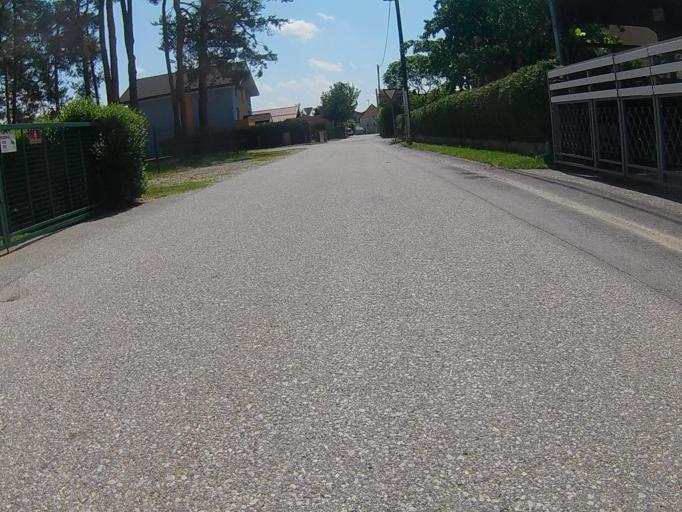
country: SI
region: Miklavz na Dravskem Polju
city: Miklavz na Dravskem Polju
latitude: 46.5108
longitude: 15.6904
